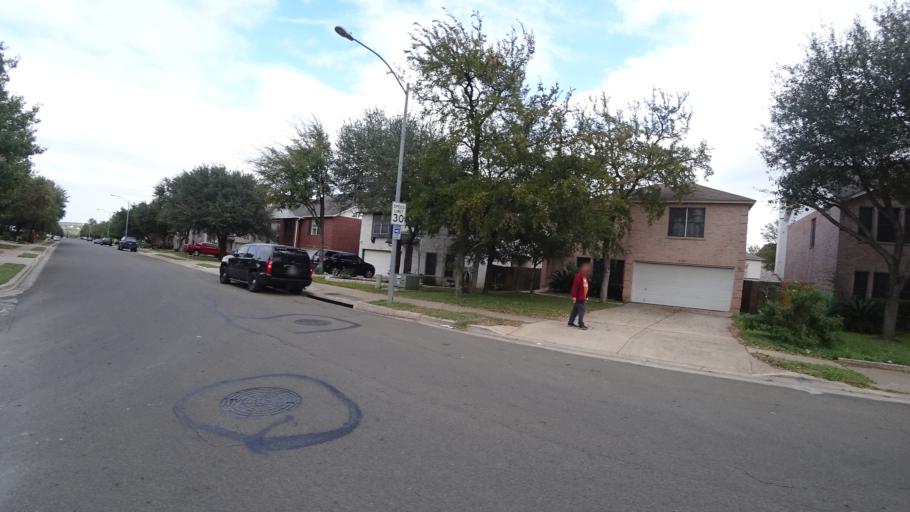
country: US
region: Texas
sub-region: Travis County
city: Manchaca
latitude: 30.1557
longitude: -97.8398
